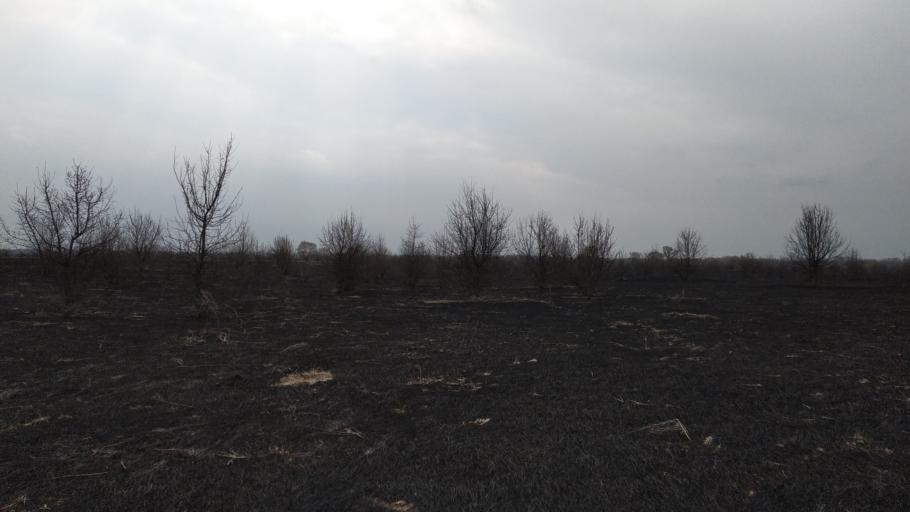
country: RU
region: Rostov
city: Semikarakorsk
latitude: 47.5527
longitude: 40.6752
